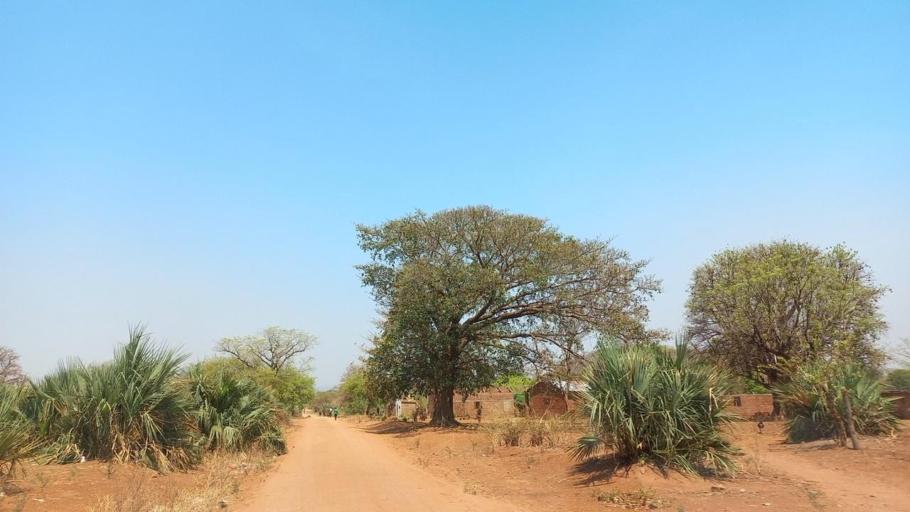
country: ZM
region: Lusaka
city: Luangwa
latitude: -15.1869
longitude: 30.2198
